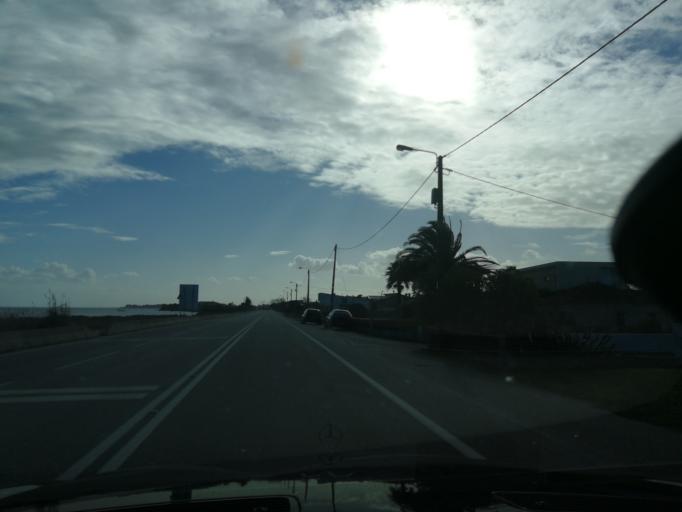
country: PT
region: Aveiro
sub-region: Murtosa
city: Murtosa
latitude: 40.7744
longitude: -8.6932
